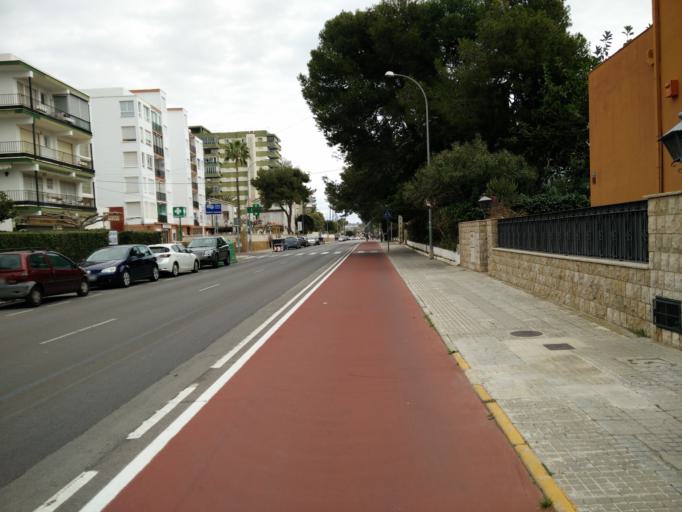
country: ES
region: Valencia
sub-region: Provincia de Castello
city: Benicassim
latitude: 40.0404
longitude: 0.0563
